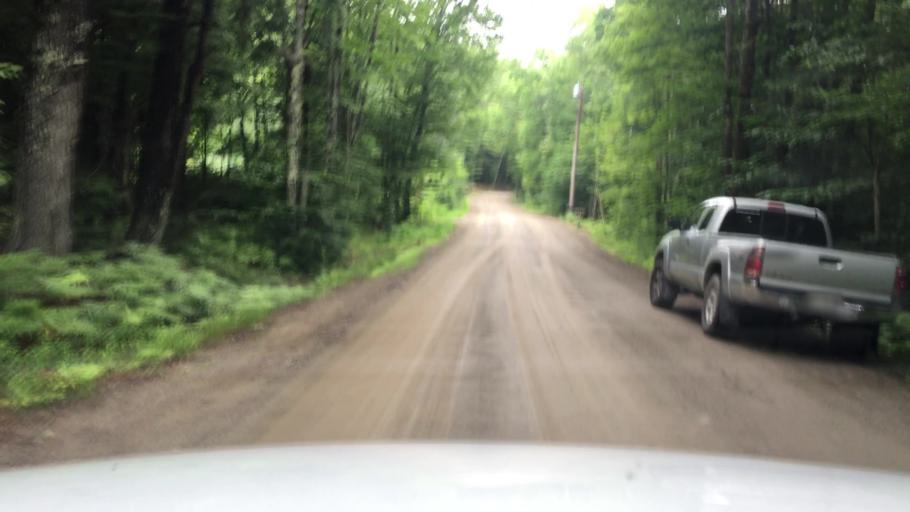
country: US
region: Maine
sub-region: Knox County
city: Hope
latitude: 44.2421
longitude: -69.1823
